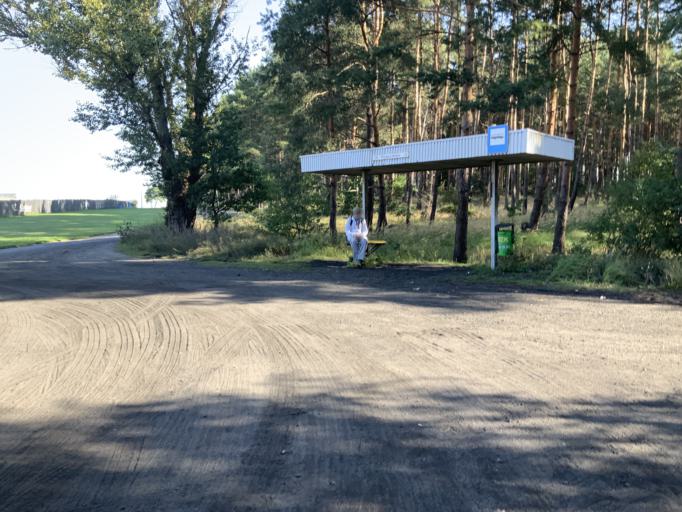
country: PL
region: Lubusz
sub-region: Zielona Gora
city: Zielona Gora
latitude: 51.9739
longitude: 15.4654
